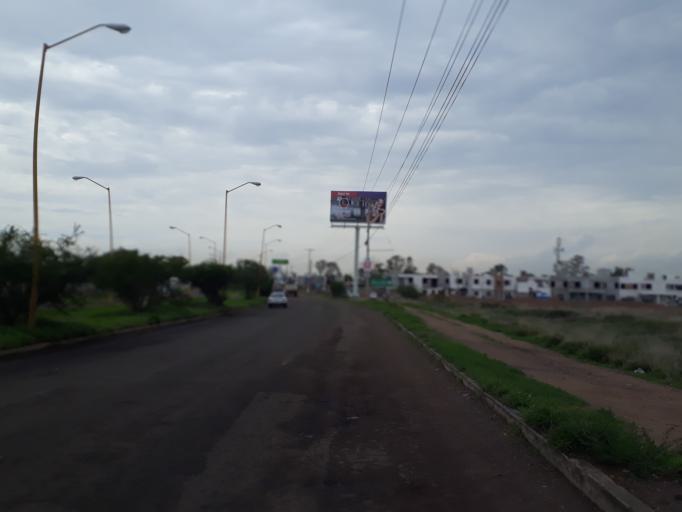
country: MX
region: Aguascalientes
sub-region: Aguascalientes
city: La Loma de los Negritos
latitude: 21.8439
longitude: -102.3276
